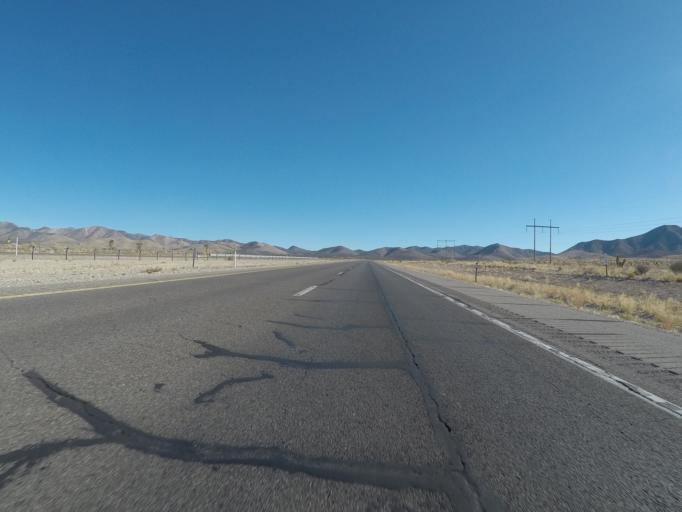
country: US
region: Nevada
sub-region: Clark County
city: Sandy Valley
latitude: 36.0195
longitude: -115.5579
